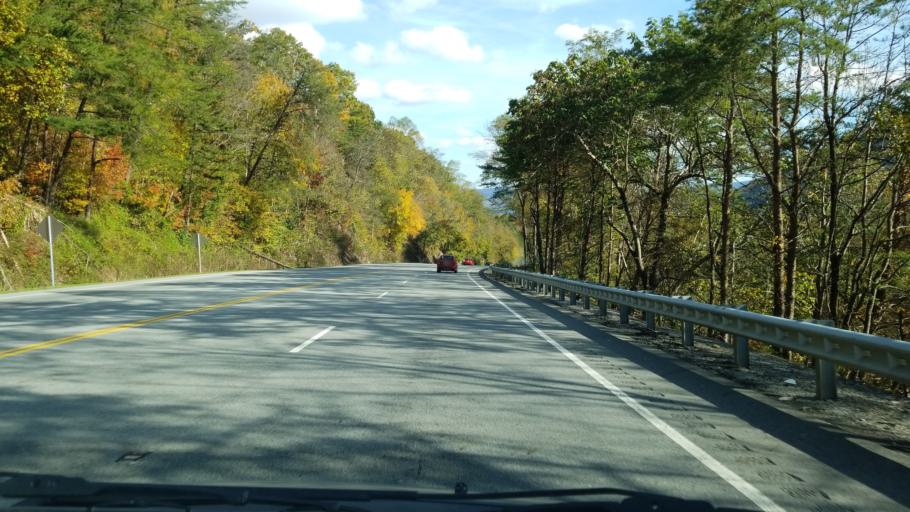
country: US
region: Tennessee
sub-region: Sequatchie County
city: Dunlap
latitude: 35.4117
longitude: -85.4093
